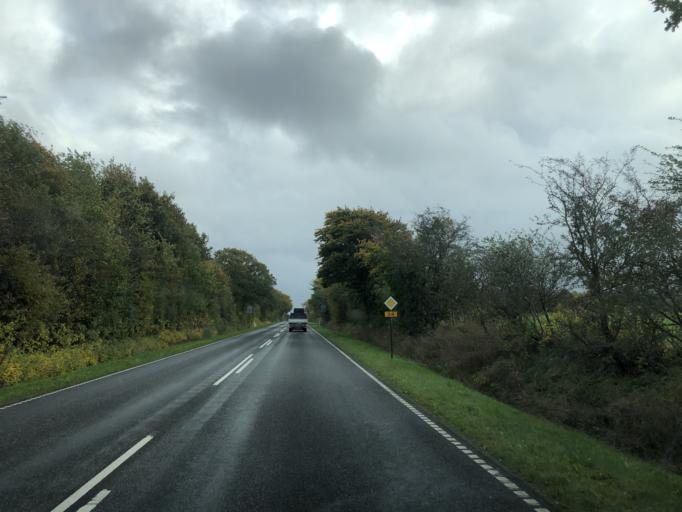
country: DK
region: South Denmark
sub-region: Haderslev Kommune
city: Vojens
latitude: 55.1957
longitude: 9.2022
